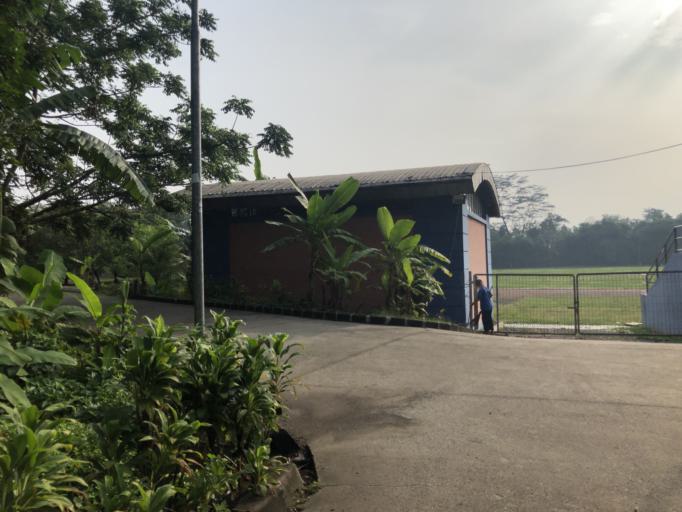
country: ID
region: West Java
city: Ciampea
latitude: -6.5569
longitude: 106.7332
